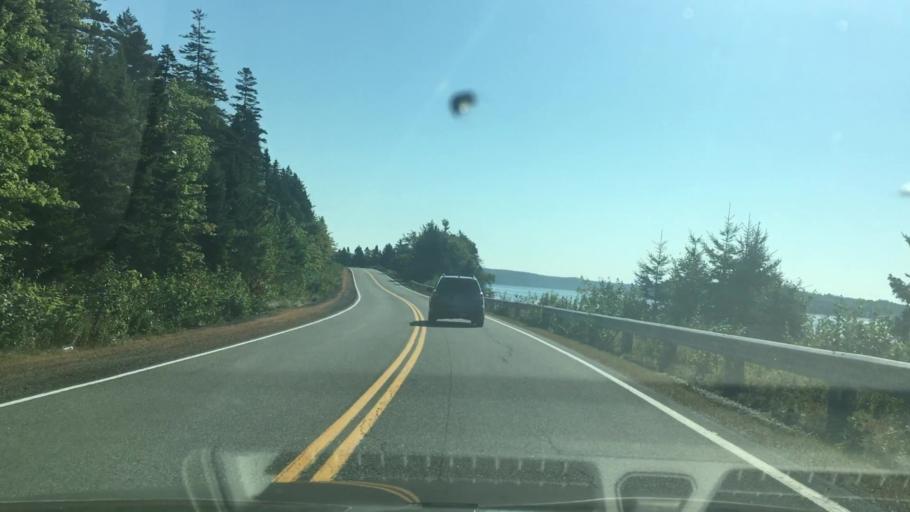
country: CA
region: Nova Scotia
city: Cole Harbour
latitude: 44.8144
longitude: -62.8741
